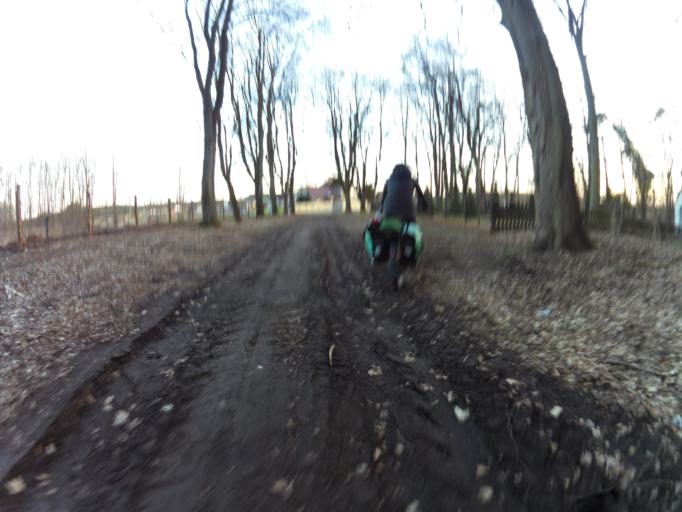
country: PL
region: West Pomeranian Voivodeship
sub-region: Powiat mysliborski
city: Debno
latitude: 52.8182
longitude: 14.7867
